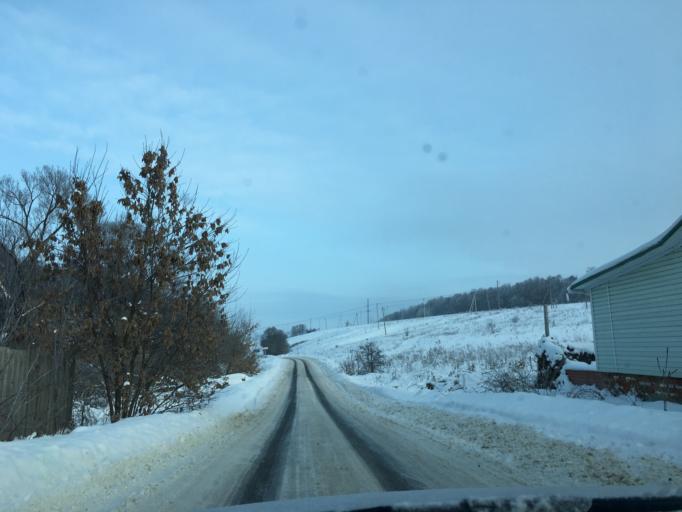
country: RU
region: Belgorod
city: Severnyy
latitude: 50.7254
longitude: 36.6115
